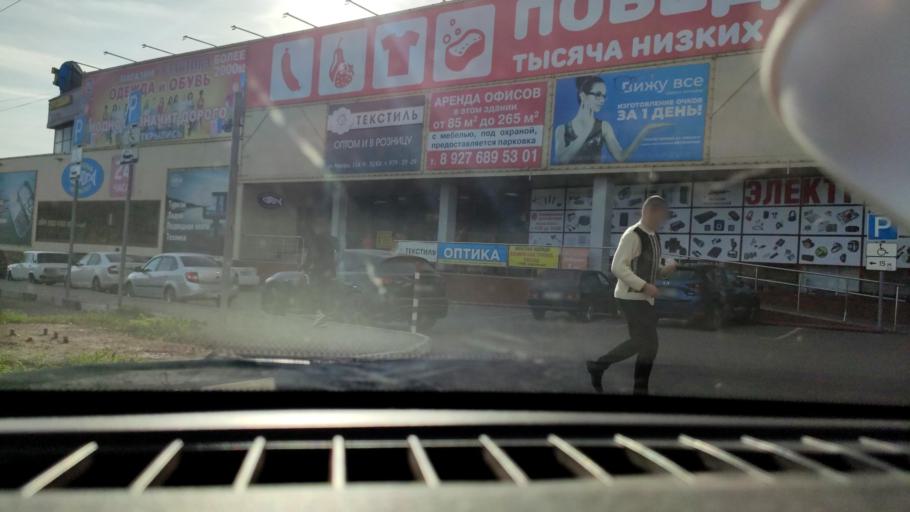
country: RU
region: Samara
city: Samara
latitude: 53.1984
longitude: 50.1903
